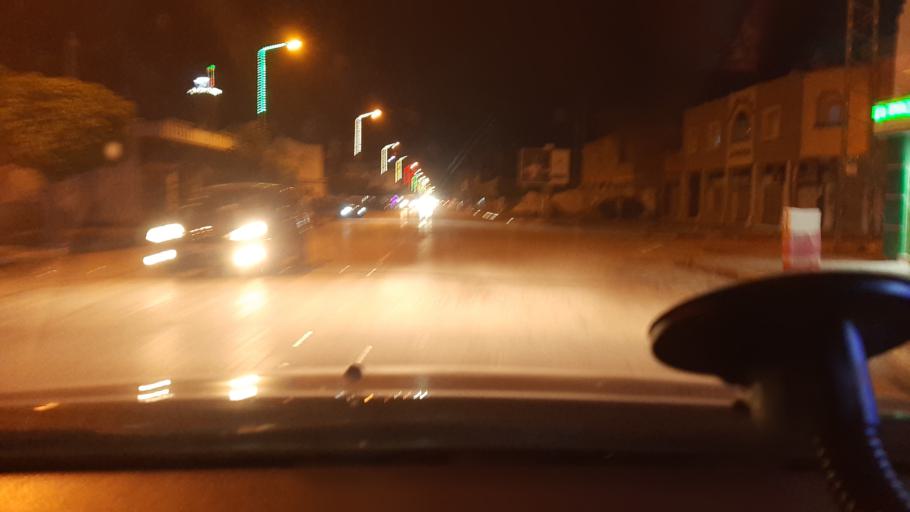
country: TN
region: Safaqis
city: Sfax
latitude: 34.7795
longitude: 10.7250
